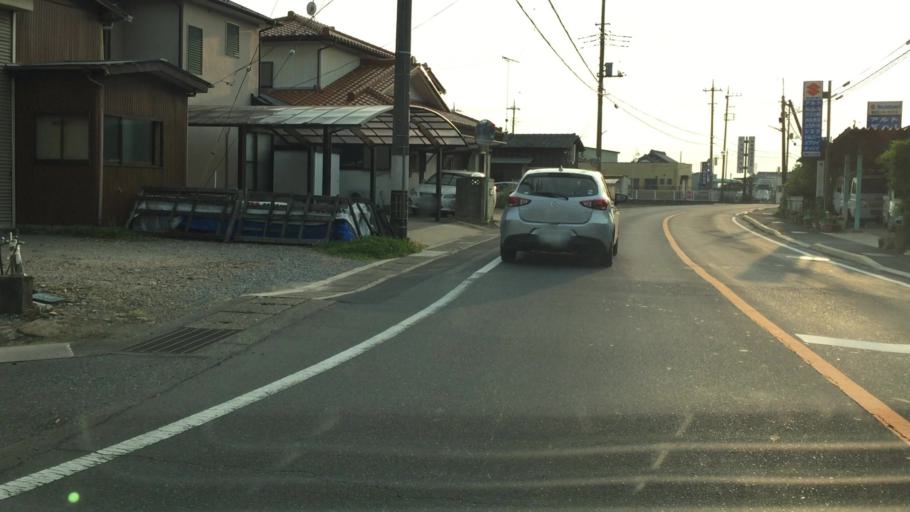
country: JP
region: Gunma
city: Tatebayashi
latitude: 36.2243
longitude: 139.5875
